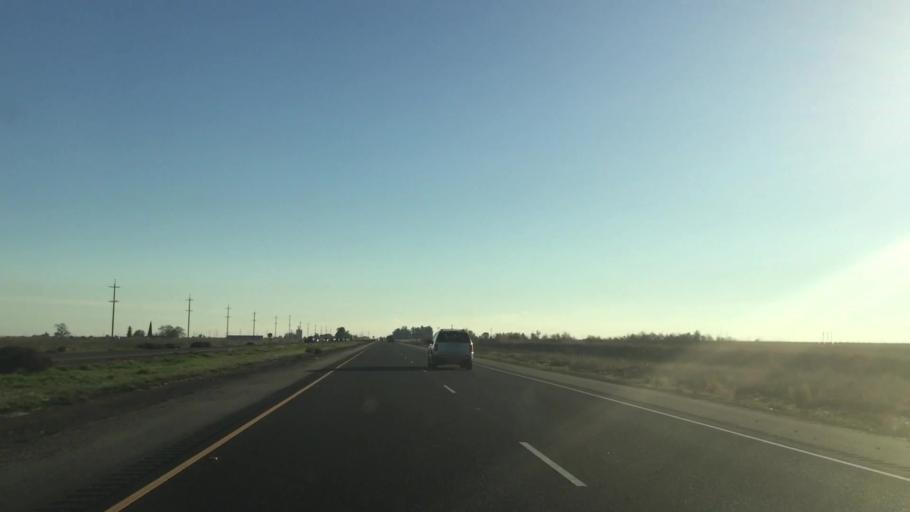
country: US
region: California
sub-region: Yuba County
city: Plumas Lake
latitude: 38.8839
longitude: -121.5434
